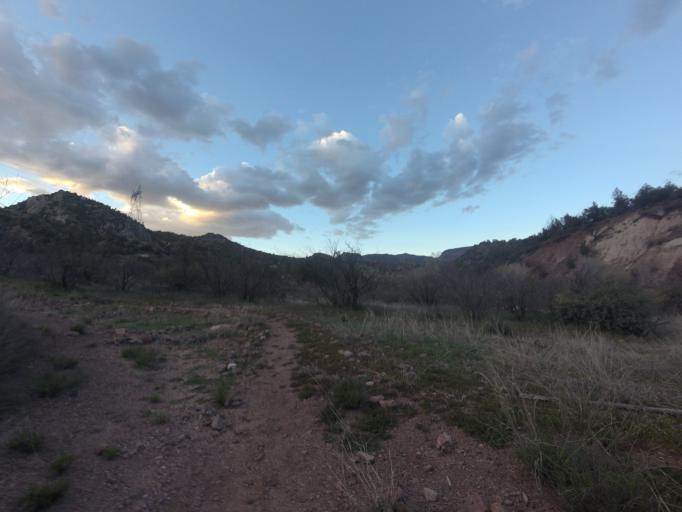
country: US
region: Arizona
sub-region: Gila County
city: Pine
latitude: 34.3800
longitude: -111.6592
